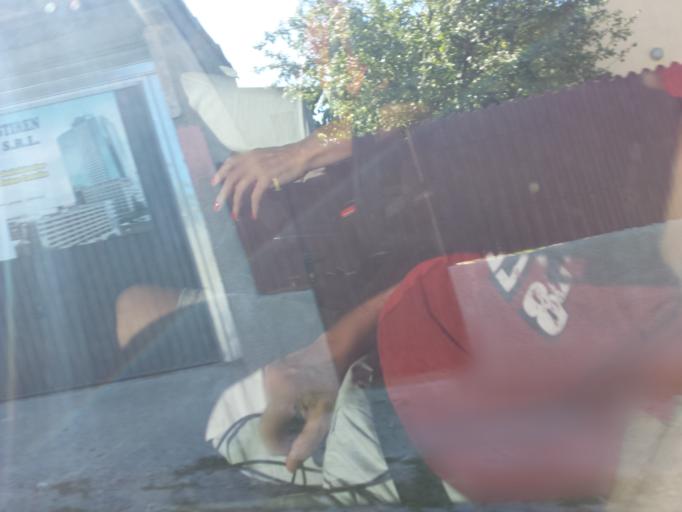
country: RO
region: Tulcea
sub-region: Municipiul Tulcea
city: Tulcea
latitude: 45.1691
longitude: 28.7903
